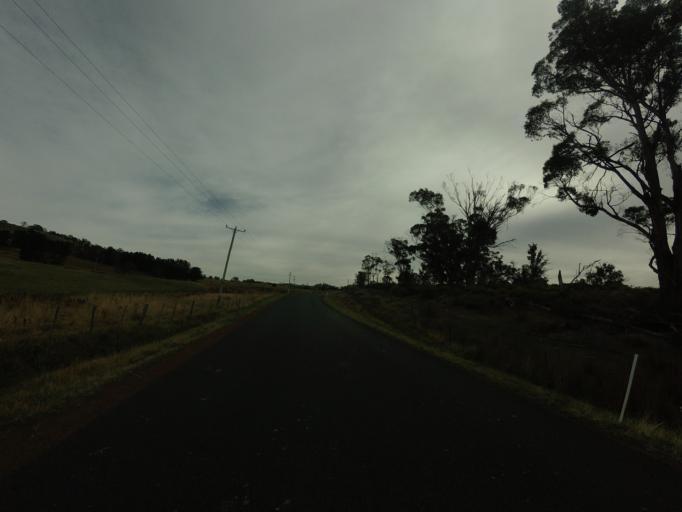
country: AU
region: Tasmania
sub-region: Sorell
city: Sorell
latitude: -42.4590
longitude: 147.5732
